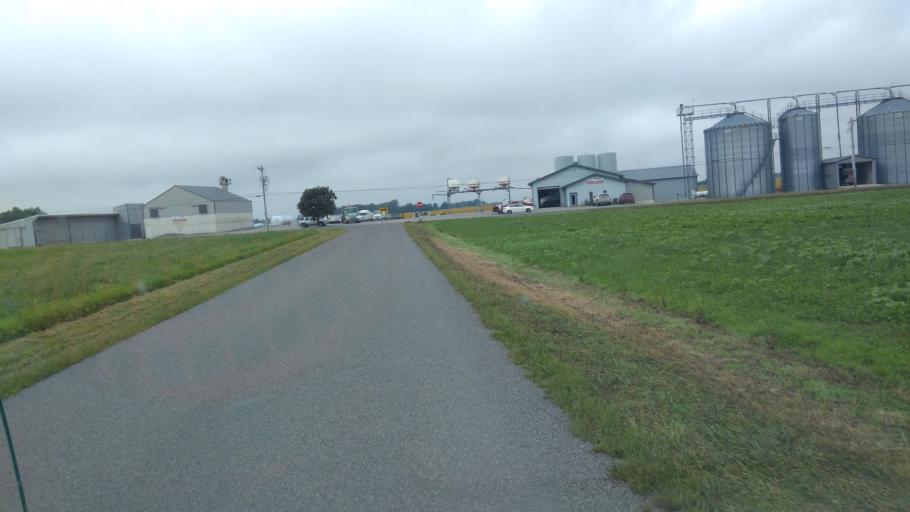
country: US
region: Ohio
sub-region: Hardin County
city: Kenton
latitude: 40.5779
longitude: -83.6842
